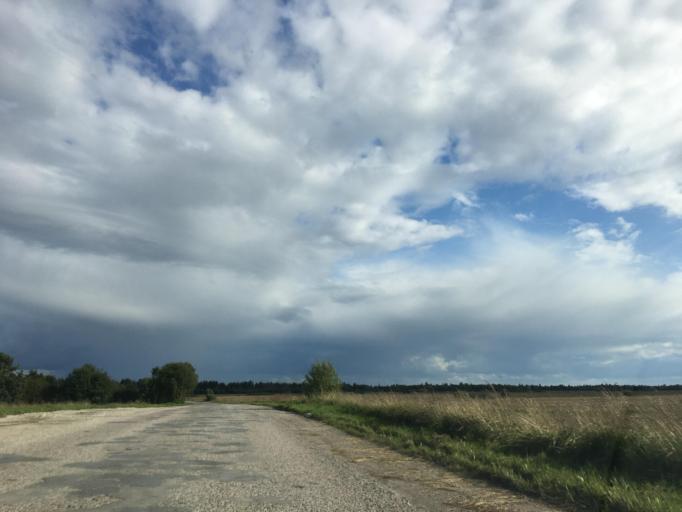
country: RU
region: Pskov
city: Izborsk
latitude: 57.7598
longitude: 27.9474
